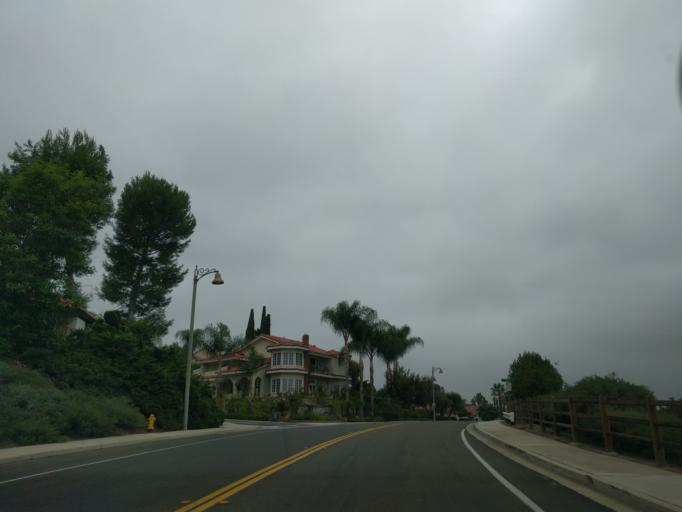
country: US
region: California
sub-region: Orange County
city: Mission Viejo
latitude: 33.5836
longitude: -117.6662
